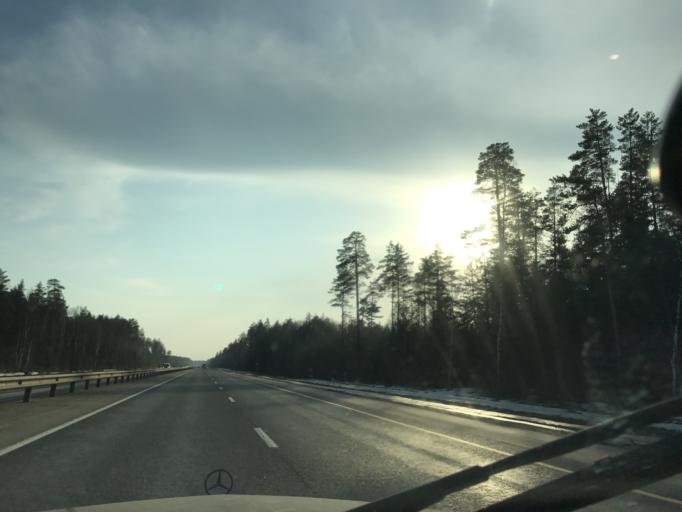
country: RU
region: Vladimir
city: Kameshkovo
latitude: 56.1726
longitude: 40.9417
